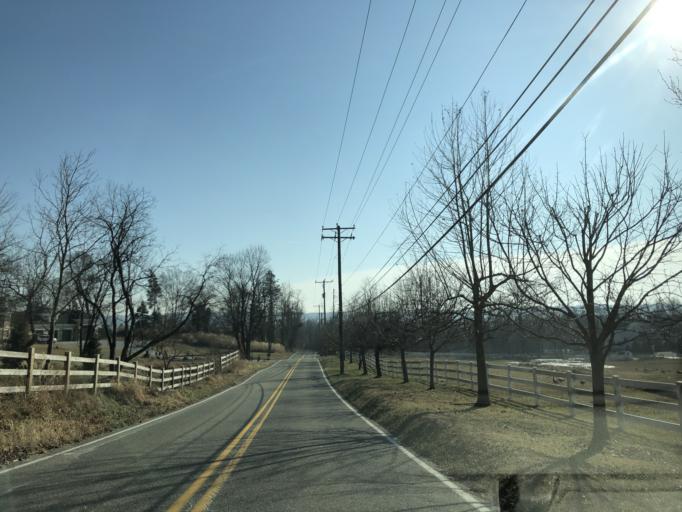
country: US
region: Pennsylvania
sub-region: Chester County
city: Chesterbrook
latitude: 40.0796
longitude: -75.4851
